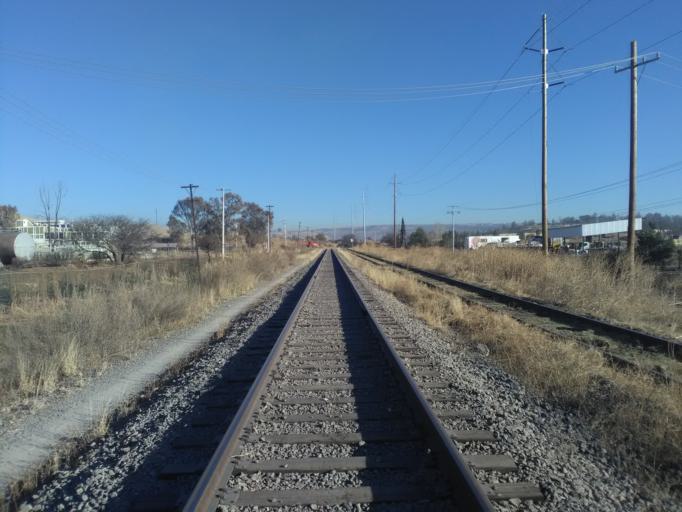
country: MX
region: Durango
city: Victoria de Durango
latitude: 24.0605
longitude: -104.6540
